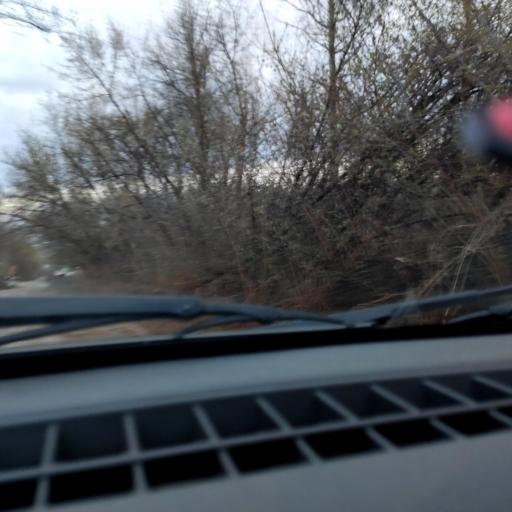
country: RU
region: Bashkortostan
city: Ufa
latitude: 54.6842
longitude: 55.9539
